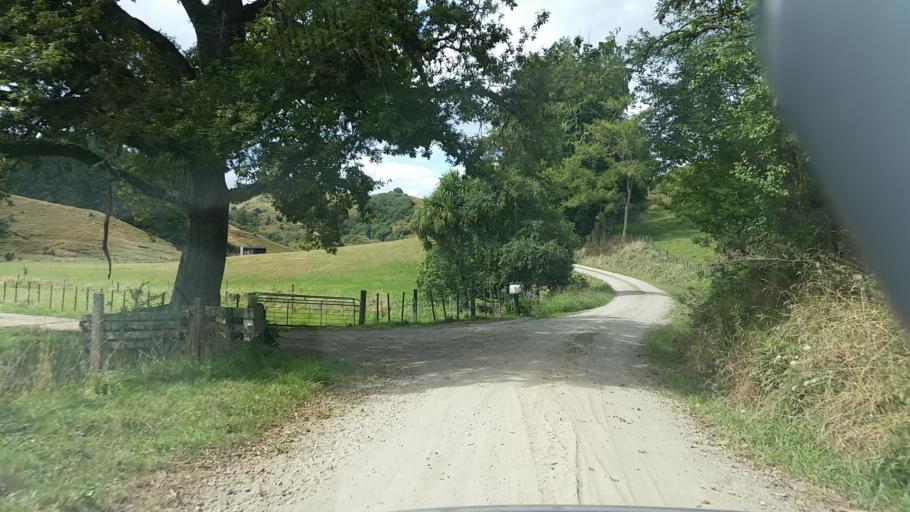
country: NZ
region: Taranaki
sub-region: South Taranaki District
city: Eltham
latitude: -39.2576
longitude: 174.5610
